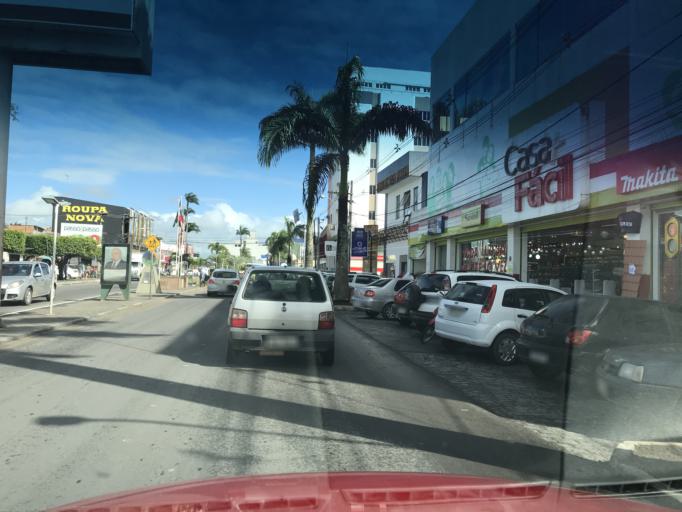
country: BR
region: Bahia
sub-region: Santo Antonio De Jesus
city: Santo Antonio de Jesus
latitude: -12.9661
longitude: -39.2634
